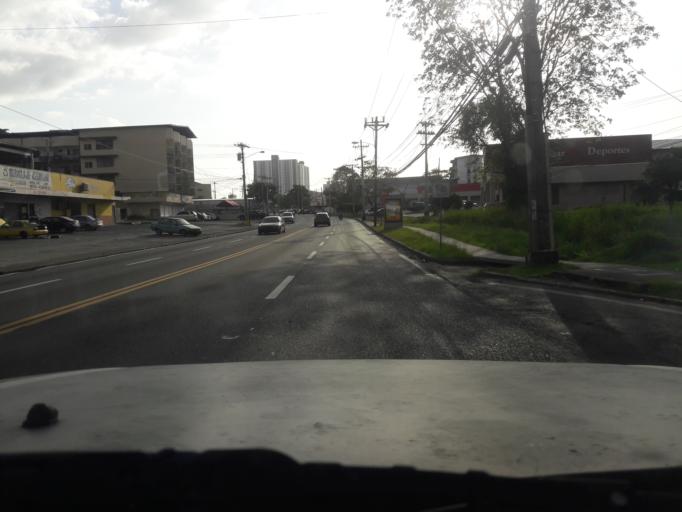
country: PA
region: Panama
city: San Miguelito
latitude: 9.0215
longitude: -79.4901
